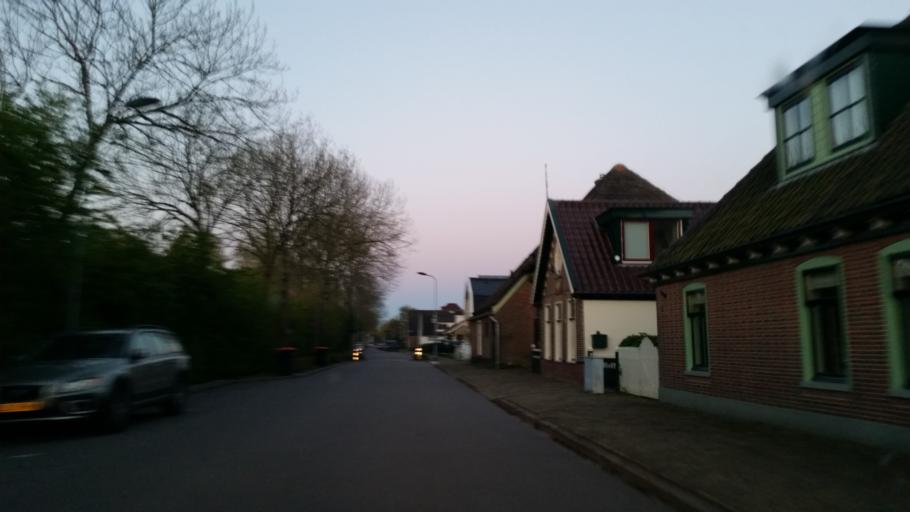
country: NL
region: North Holland
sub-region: Gemeente Schagen
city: Harenkarspel
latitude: 52.7502
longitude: 4.7724
